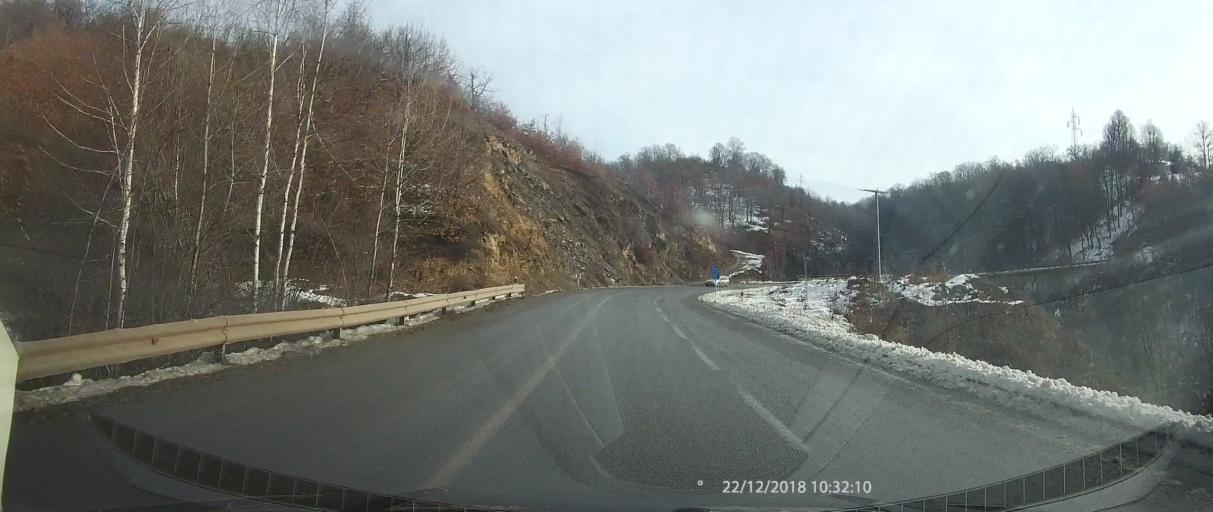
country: MK
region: Kriva Palanka
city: Kriva Palanka
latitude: 42.2209
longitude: 22.4316
